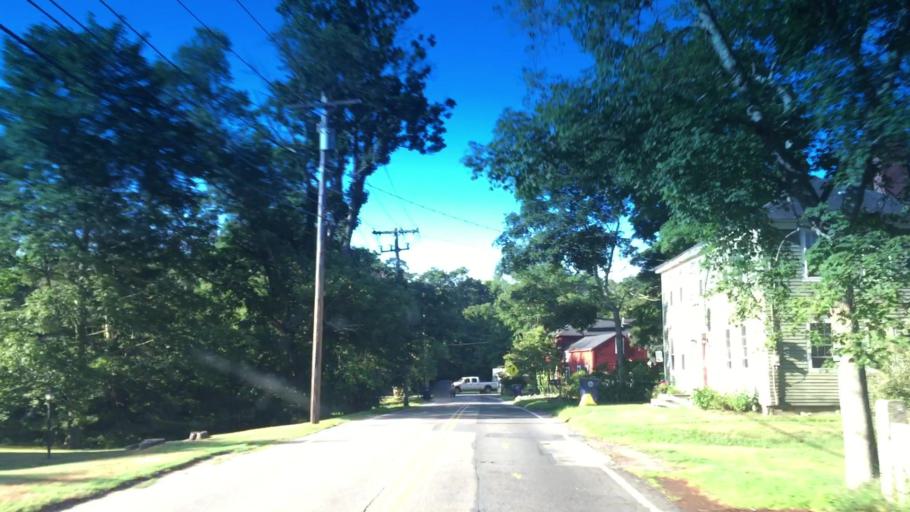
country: US
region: Massachusetts
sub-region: Norfolk County
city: Medway
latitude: 42.1414
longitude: -71.3937
